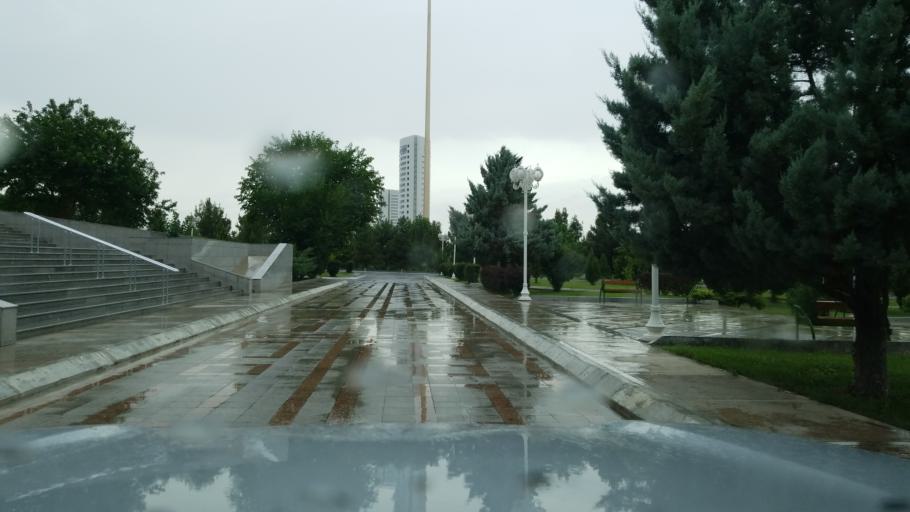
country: TM
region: Ahal
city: Ashgabat
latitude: 37.8857
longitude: 58.3530
